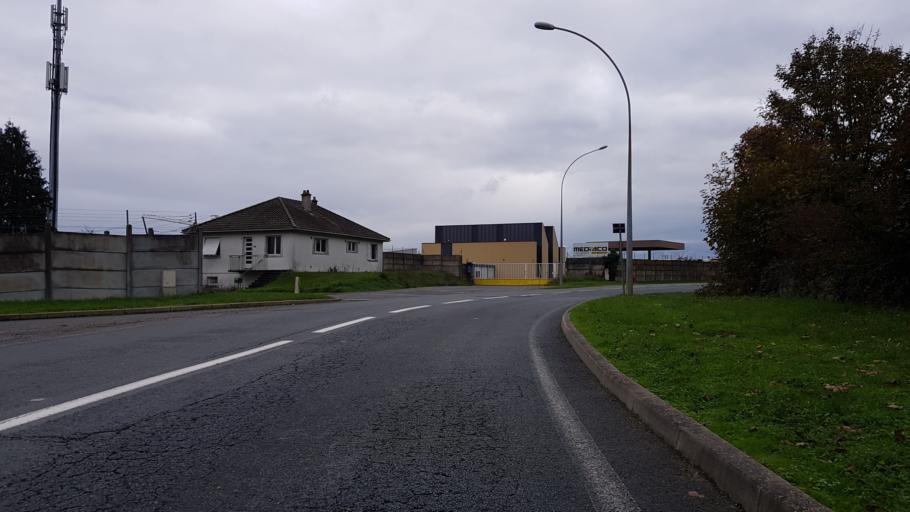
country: FR
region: Poitou-Charentes
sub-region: Departement de la Vienne
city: Chasseneuil-du-Poitou
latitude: 46.6669
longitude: 0.3760
